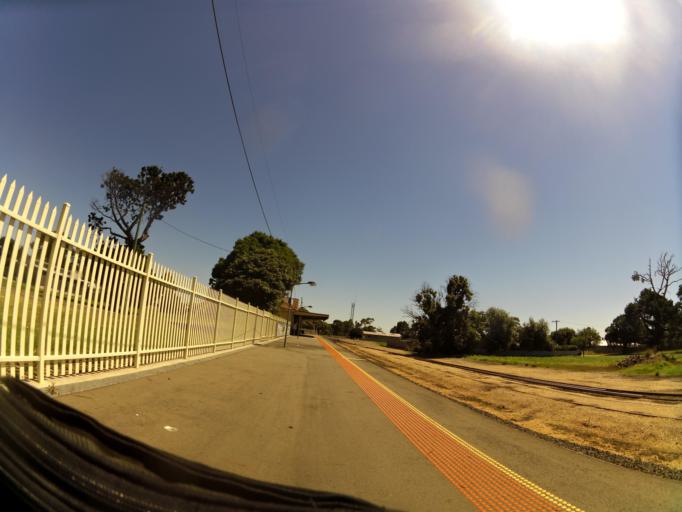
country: AU
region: Victoria
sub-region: Wellington
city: Sale
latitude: -37.9676
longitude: 147.0815
